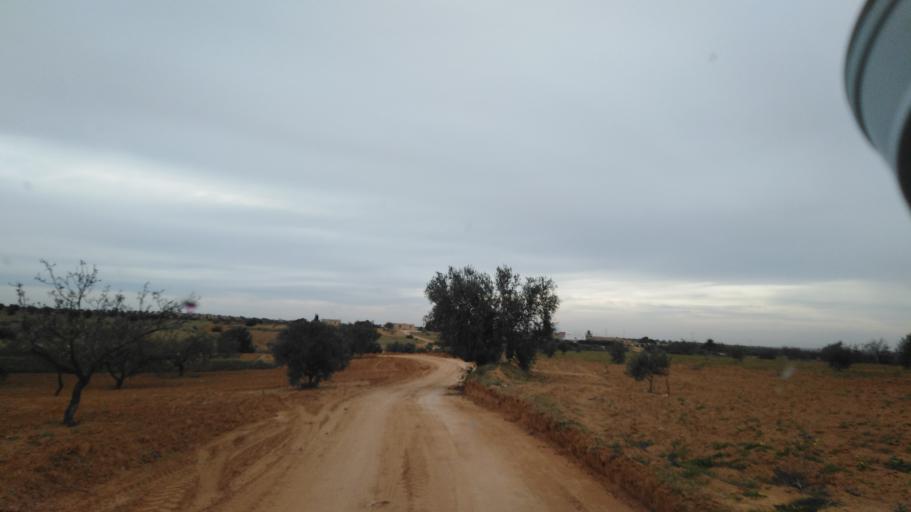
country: TN
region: Safaqis
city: Bi'r `Ali Bin Khalifah
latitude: 34.7683
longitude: 10.3748
